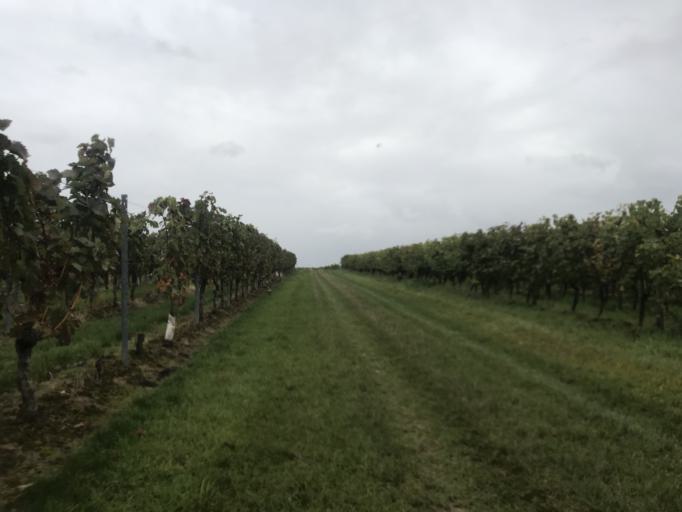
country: DE
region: Rheinland-Pfalz
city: Schwabenheim
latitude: 49.9410
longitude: 8.0997
